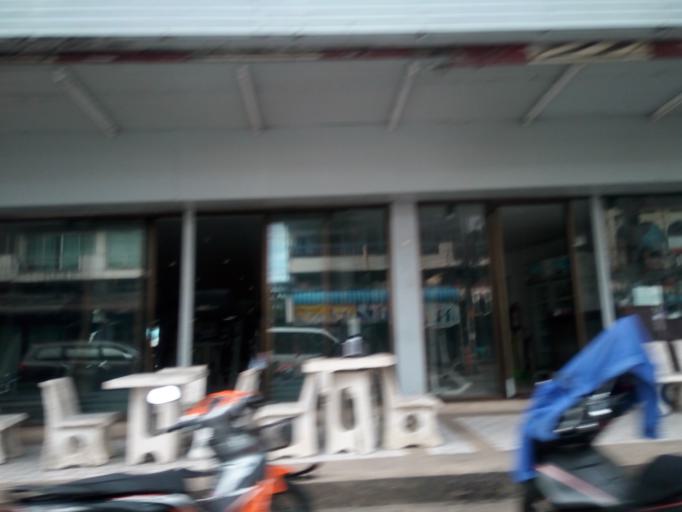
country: TH
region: Phuket
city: Ban Talat Nua
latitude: 7.8741
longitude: 98.3794
